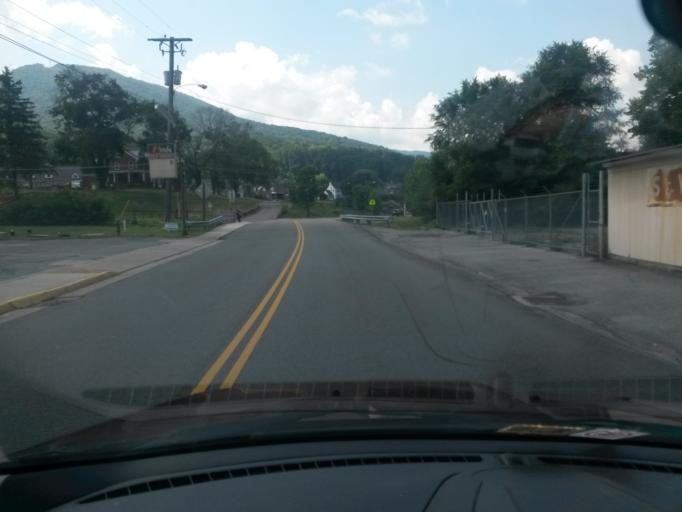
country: US
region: Virginia
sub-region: Giles County
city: Narrows
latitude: 37.3305
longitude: -80.8120
